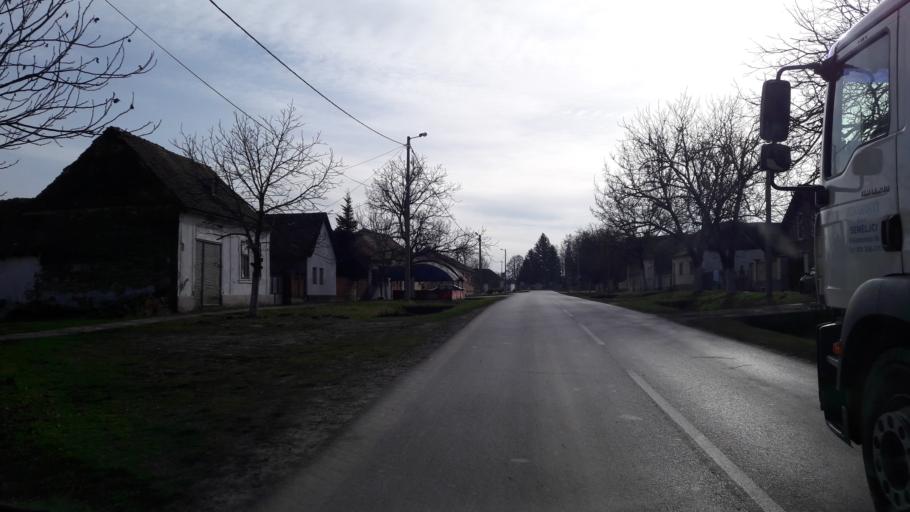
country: HR
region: Osjecko-Baranjska
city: Semeljci
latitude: 45.3542
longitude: 18.5551
